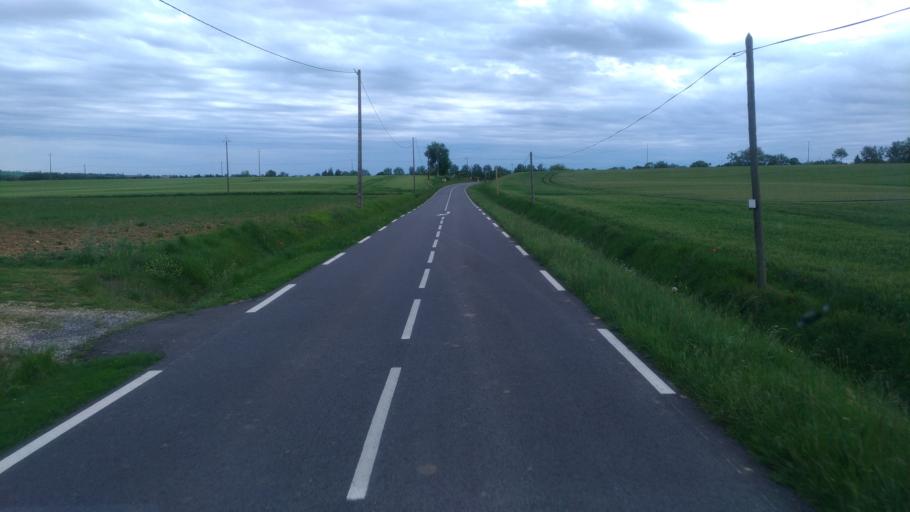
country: FR
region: Midi-Pyrenees
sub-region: Departement de la Haute-Garonne
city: Villefranche-de-Lauragais
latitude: 43.4280
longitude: 1.7661
